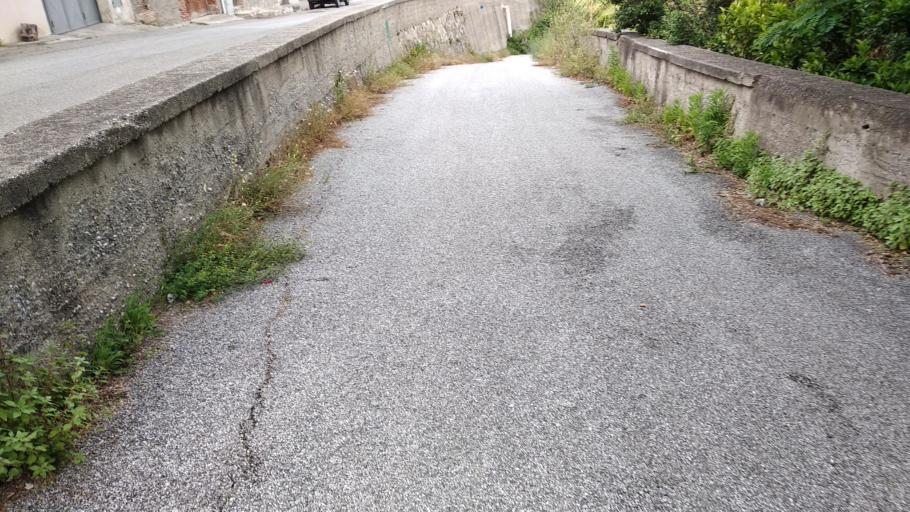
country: IT
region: Sicily
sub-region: Messina
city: Gualtieri Sicamino
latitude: 38.1605
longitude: 15.3098
